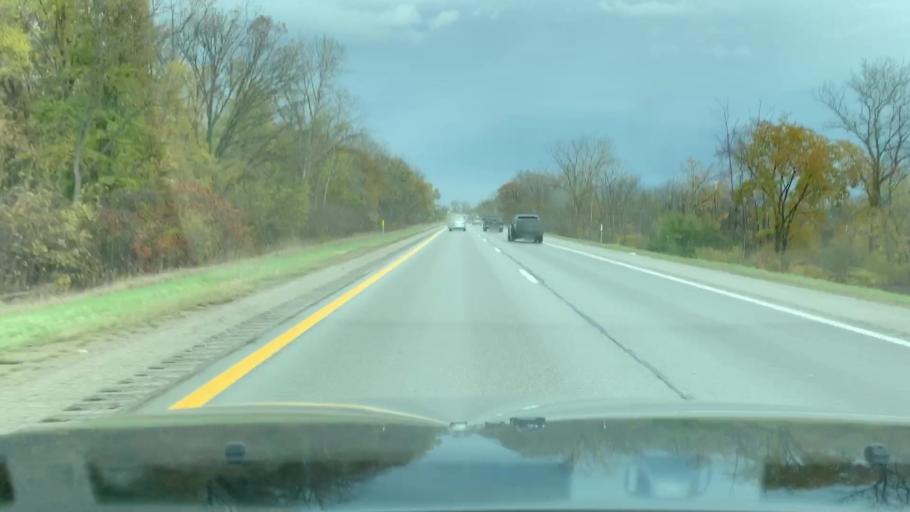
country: US
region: Michigan
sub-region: Kent County
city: Wyoming
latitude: 42.9309
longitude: -85.7332
